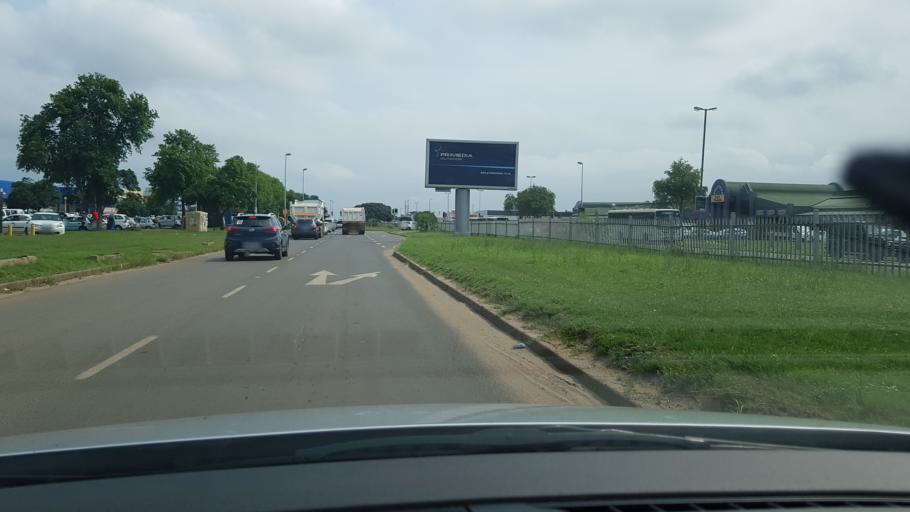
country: ZA
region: KwaZulu-Natal
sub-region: uThungulu District Municipality
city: Richards Bay
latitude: -28.7494
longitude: 32.0489
